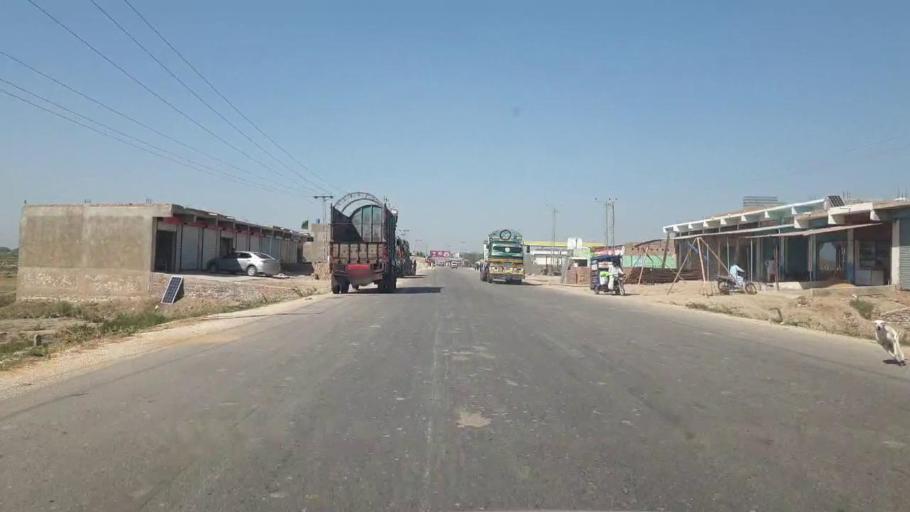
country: PK
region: Sindh
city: Talhar
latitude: 24.8815
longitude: 68.8111
